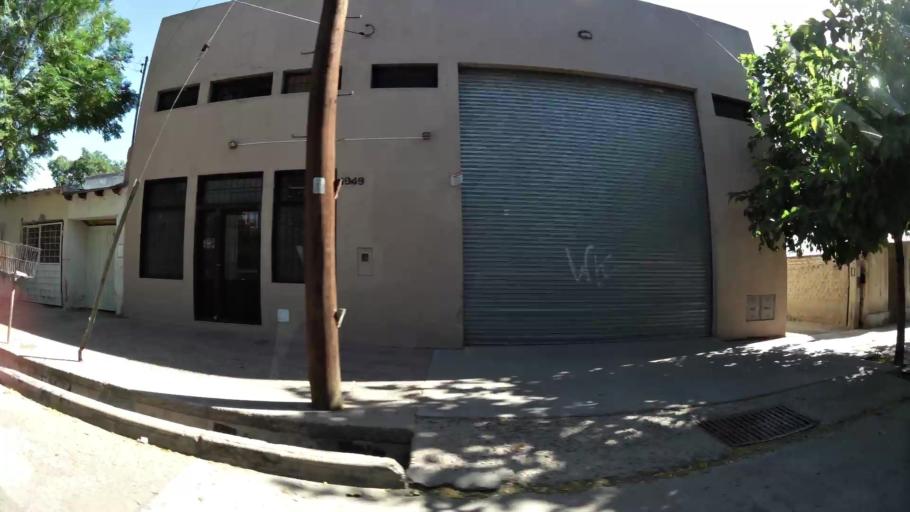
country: AR
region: Mendoza
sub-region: Departamento de Godoy Cruz
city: Godoy Cruz
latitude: -32.9245
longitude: -68.8626
